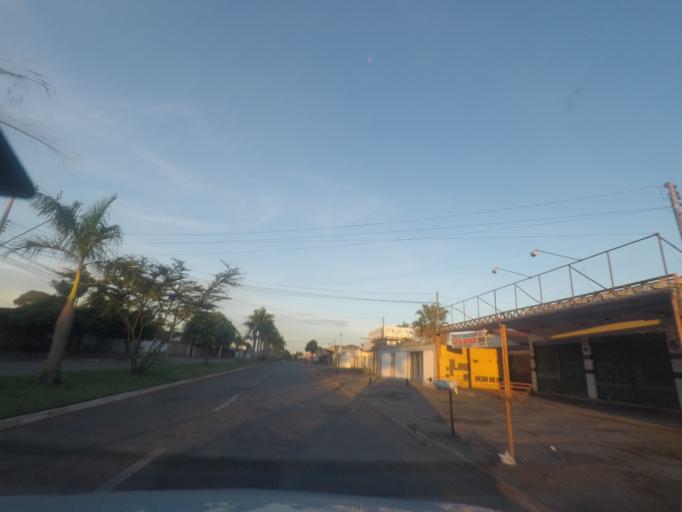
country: BR
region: Goias
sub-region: Goiania
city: Goiania
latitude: -16.6880
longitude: -49.3493
